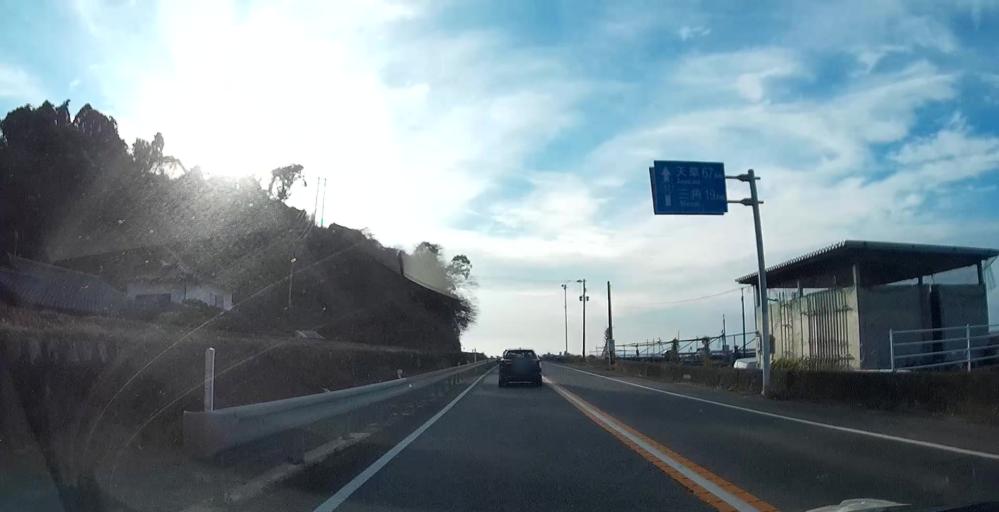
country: JP
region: Kumamoto
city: Uto
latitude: 32.7012
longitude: 130.5736
